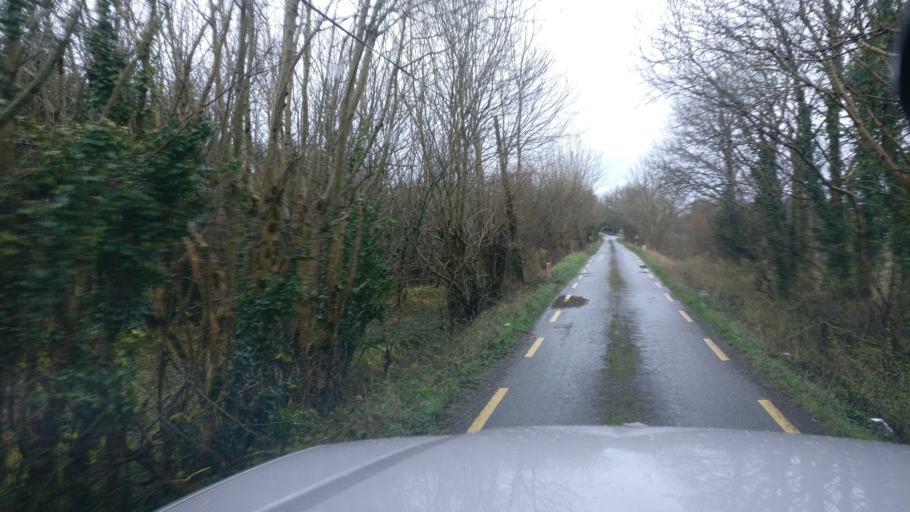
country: IE
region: Connaught
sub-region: County Galway
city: Ballinasloe
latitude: 53.2576
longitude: -8.3556
